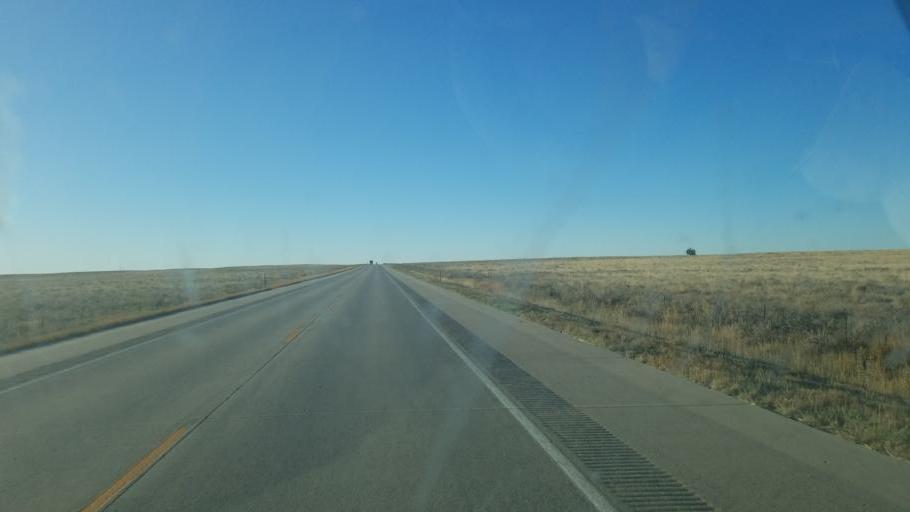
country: US
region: Colorado
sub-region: Kiowa County
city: Eads
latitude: 38.5523
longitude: -102.7861
